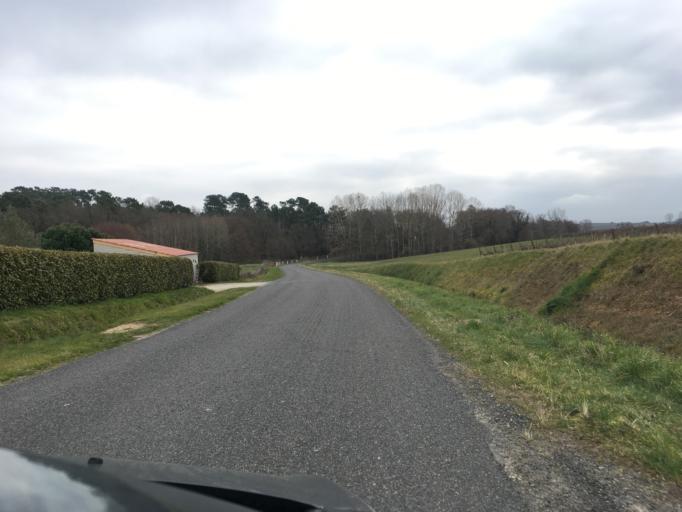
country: FR
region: Poitou-Charentes
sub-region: Departement de la Charente-Maritime
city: Mirambeau
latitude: 45.3299
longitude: -0.5856
